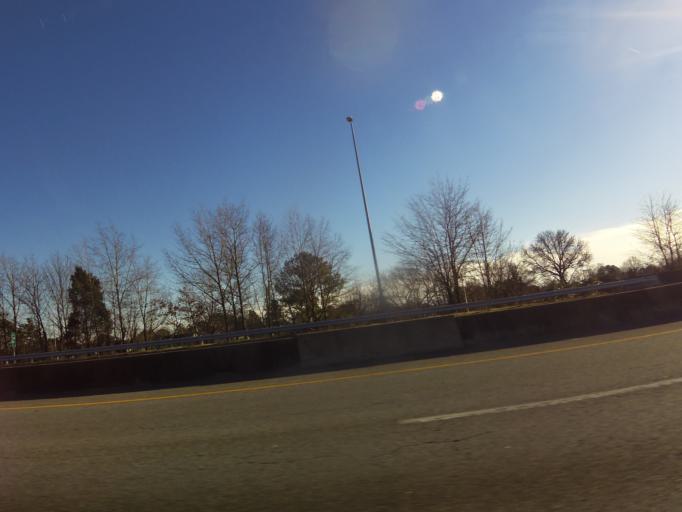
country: US
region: Virginia
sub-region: City of Portsmouth
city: Portsmouth Heights
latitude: 36.8219
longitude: -76.3351
